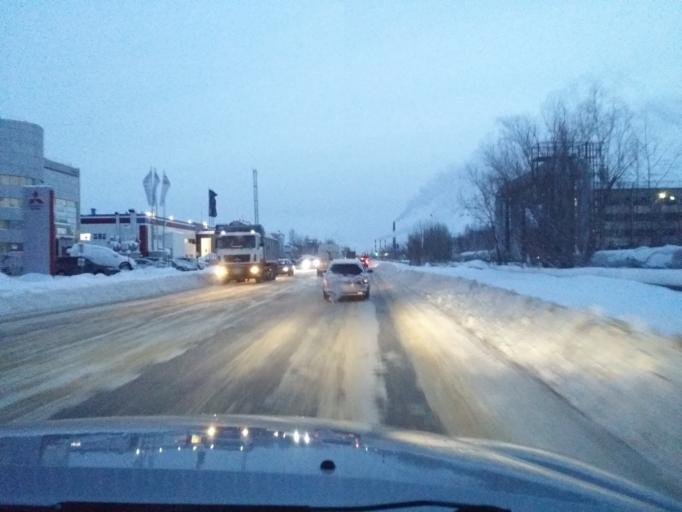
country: RU
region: Khanty-Mansiyskiy Avtonomnyy Okrug
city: Nizhnevartovsk
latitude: 60.9470
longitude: 76.5480
